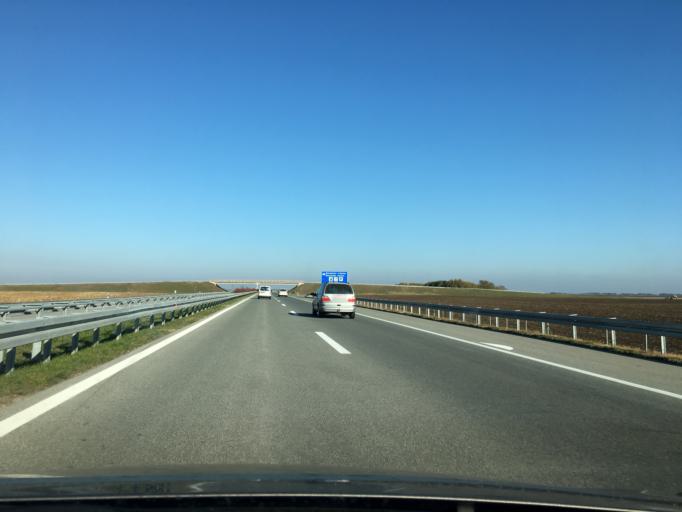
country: RS
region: Autonomna Pokrajina Vojvodina
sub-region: Severnobacki Okrug
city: Mali Igos
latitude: 45.7453
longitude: 19.7027
